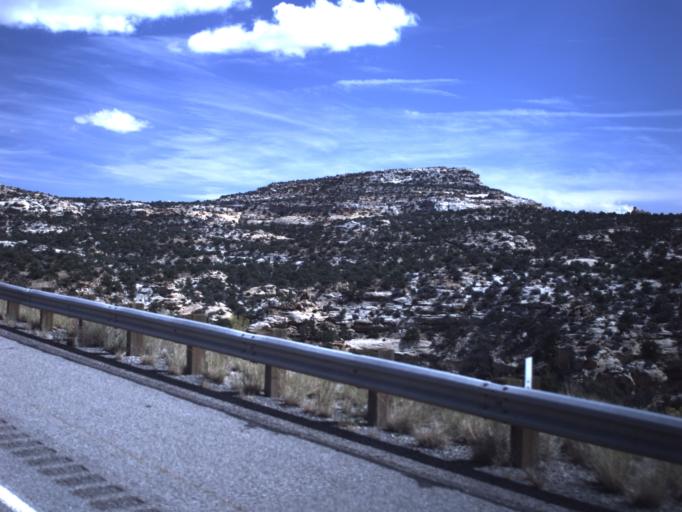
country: US
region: Utah
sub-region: Emery County
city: Ferron
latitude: 38.8593
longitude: -110.8226
